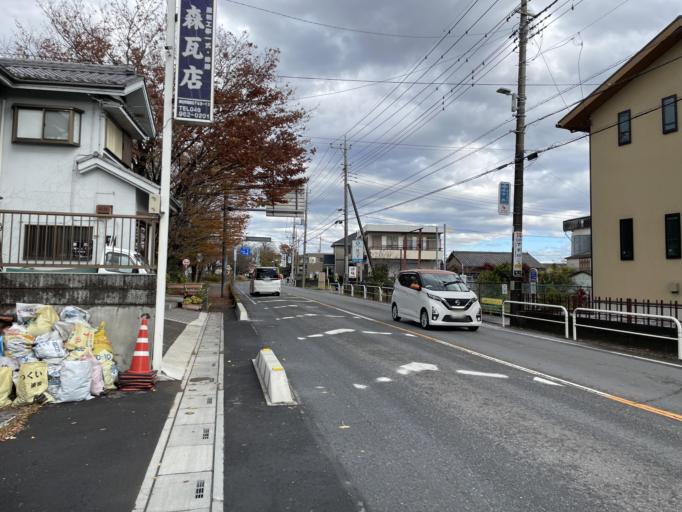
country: JP
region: Saitama
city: Koshigaya
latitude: 35.9167
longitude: 139.8039
